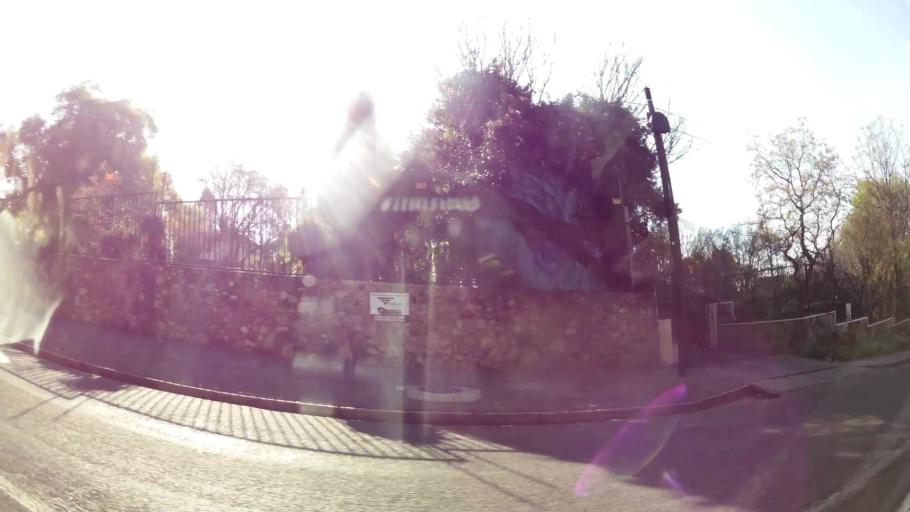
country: ZA
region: Gauteng
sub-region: City of Johannesburg Metropolitan Municipality
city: Johannesburg
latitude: -26.1696
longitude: 28.0871
